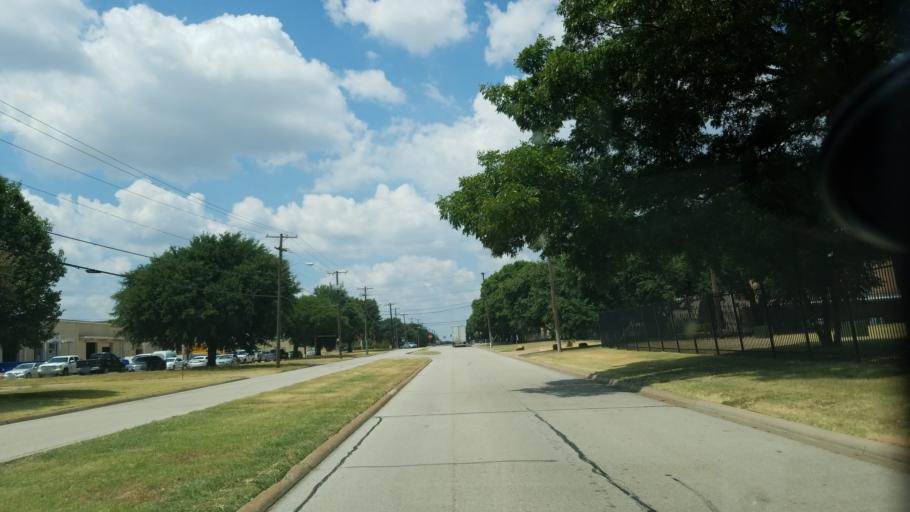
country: US
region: Texas
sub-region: Dallas County
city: Duncanville
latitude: 32.6872
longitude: -96.8895
